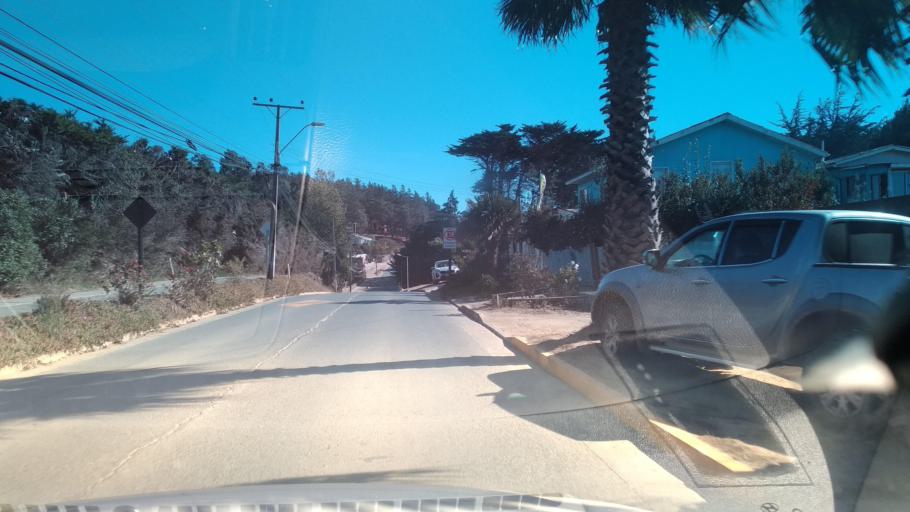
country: CL
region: O'Higgins
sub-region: Provincia de Colchagua
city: Santa Cruz
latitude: -34.3926
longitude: -72.0082
